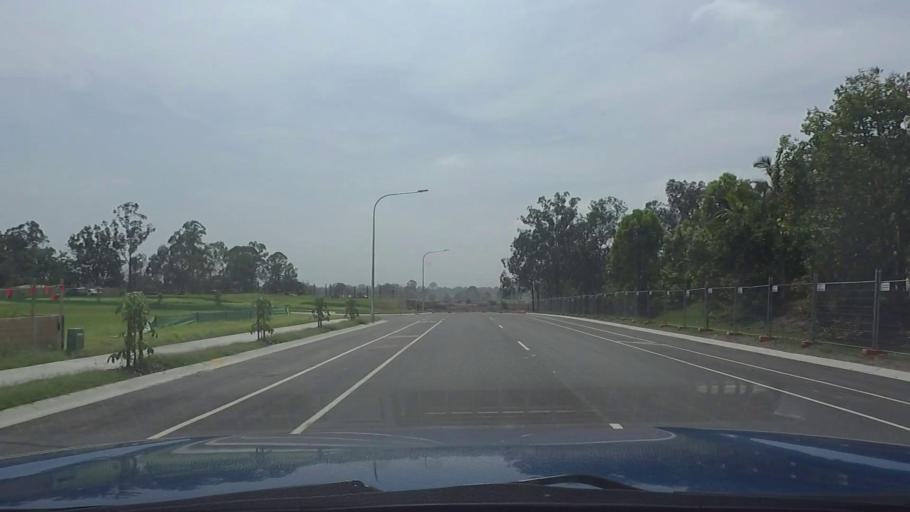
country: AU
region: Queensland
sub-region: Logan
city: Logan Reserve
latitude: -27.7041
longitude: 153.1077
